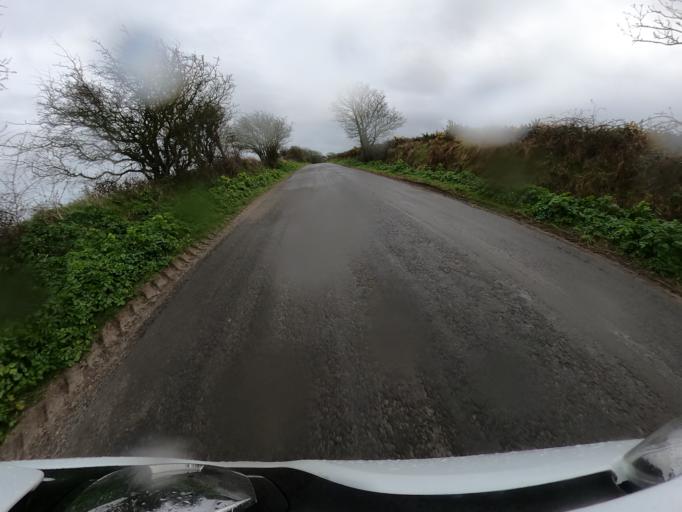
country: IM
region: Ramsey
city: Ramsey
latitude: 54.3683
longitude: -4.4557
